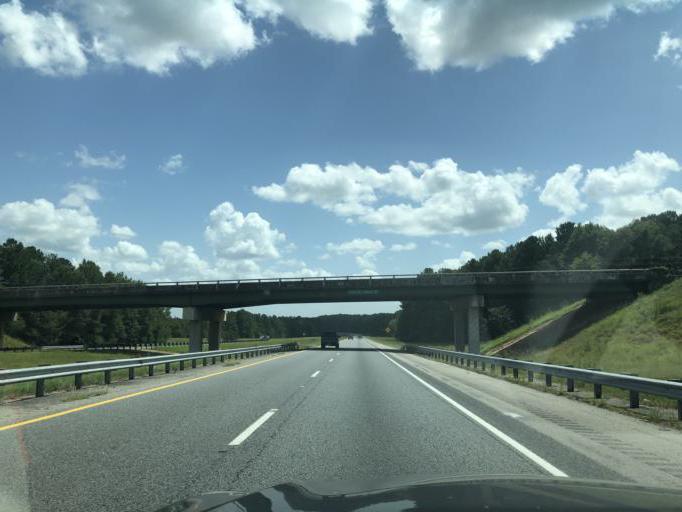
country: US
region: Georgia
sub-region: Troup County
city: La Grange
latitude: 33.0130
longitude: -84.9528
